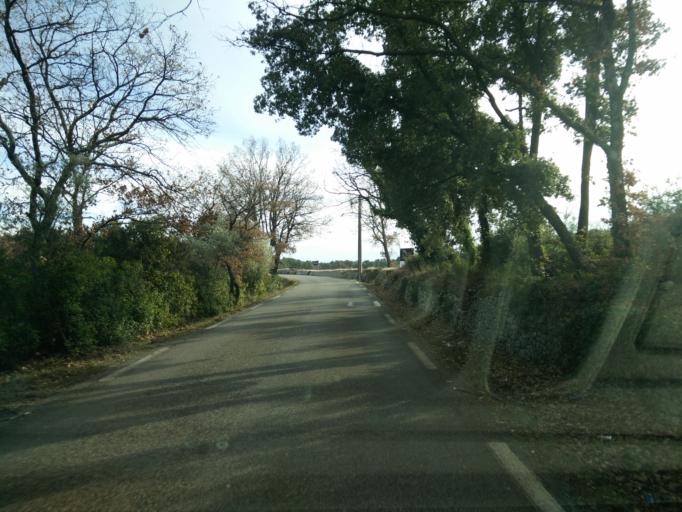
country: FR
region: Provence-Alpes-Cote d'Azur
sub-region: Departement du Var
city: Lorgues
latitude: 43.4656
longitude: 6.3888
